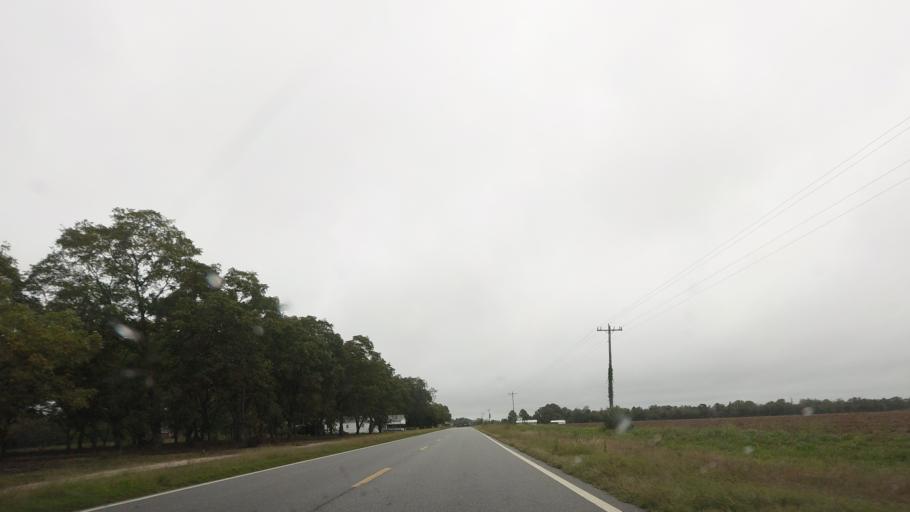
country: US
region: Georgia
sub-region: Berrien County
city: Enigma
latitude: 31.4710
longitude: -83.2377
